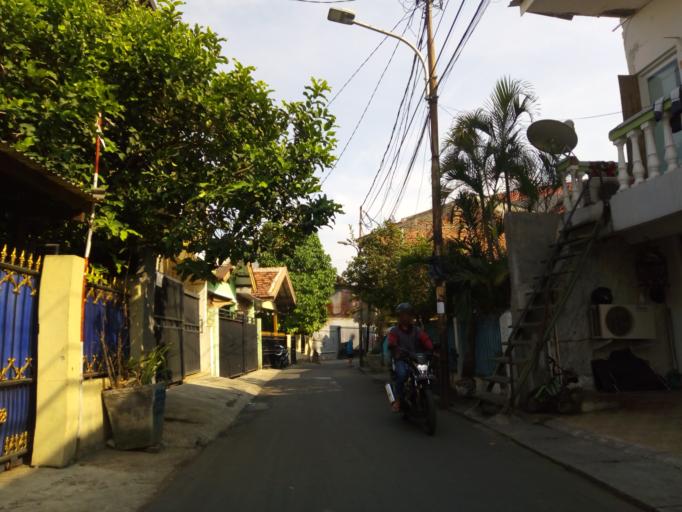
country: ID
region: Jakarta Raya
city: Jakarta
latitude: -6.2104
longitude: 106.8397
